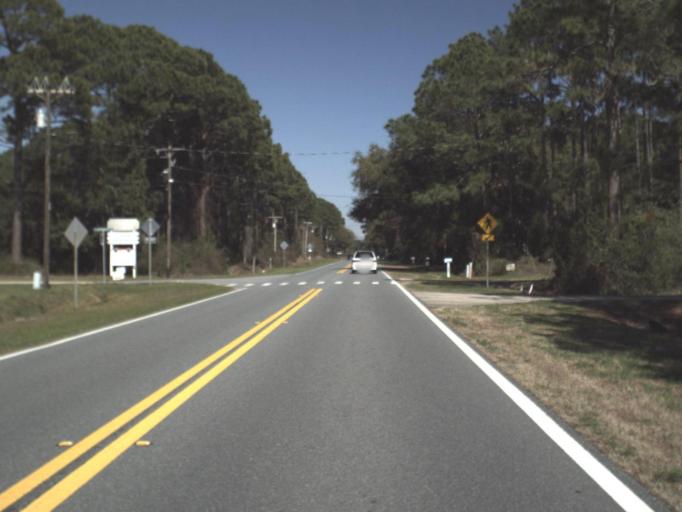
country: US
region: Florida
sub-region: Franklin County
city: Carrabelle
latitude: 29.8826
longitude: -84.5921
